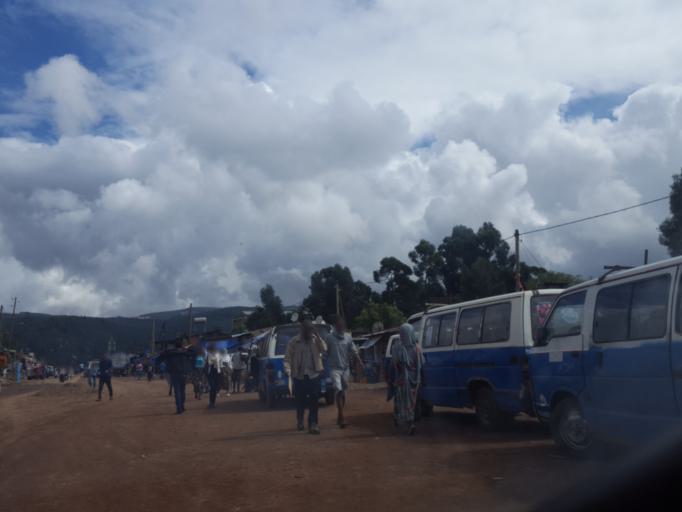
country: ET
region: Adis Abeba
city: Addis Ababa
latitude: 9.0637
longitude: 38.7616
